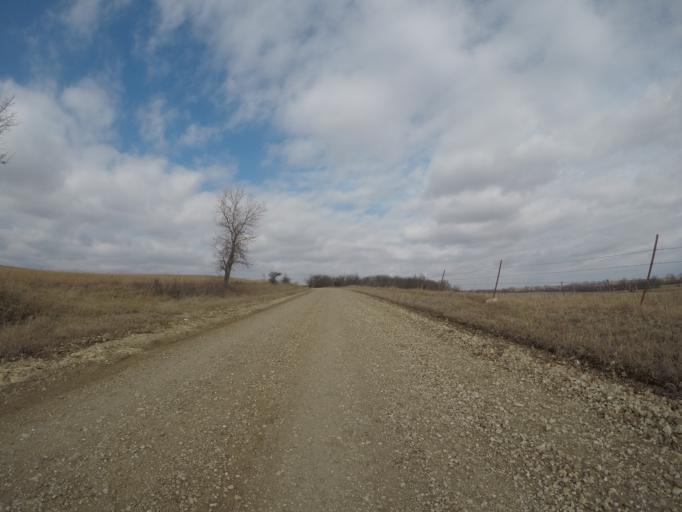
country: US
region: Kansas
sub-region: Morris County
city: Council Grove
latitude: 38.7740
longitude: -96.3527
